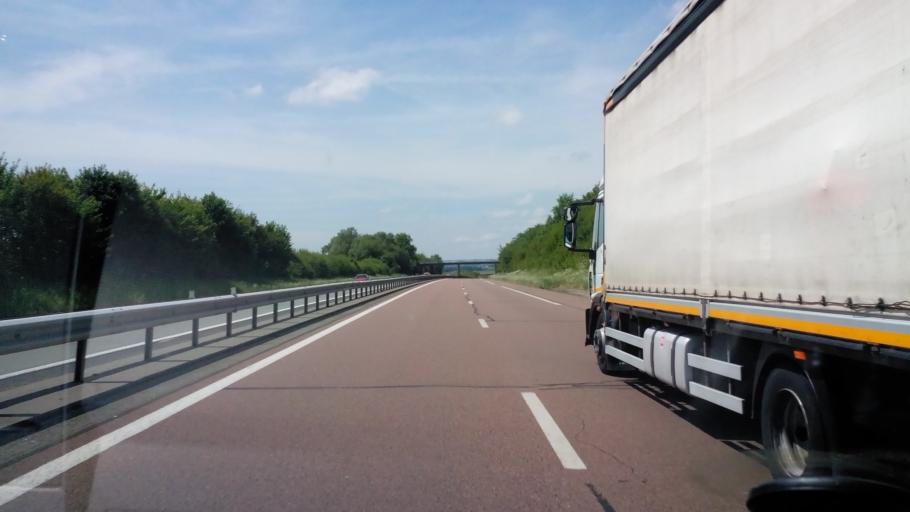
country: FR
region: Champagne-Ardenne
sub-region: Departement de la Haute-Marne
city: Avrecourt
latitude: 48.0464
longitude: 5.5715
